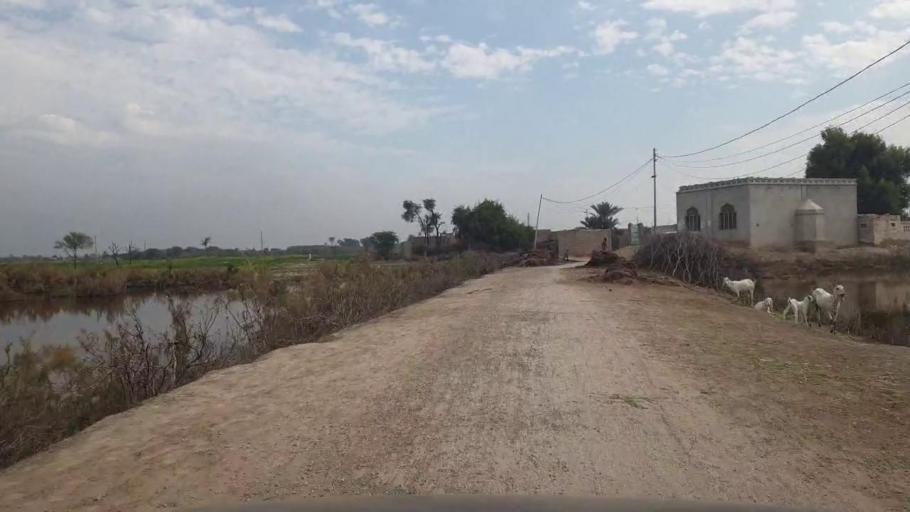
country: PK
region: Sindh
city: Sakrand
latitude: 26.0258
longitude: 68.4022
